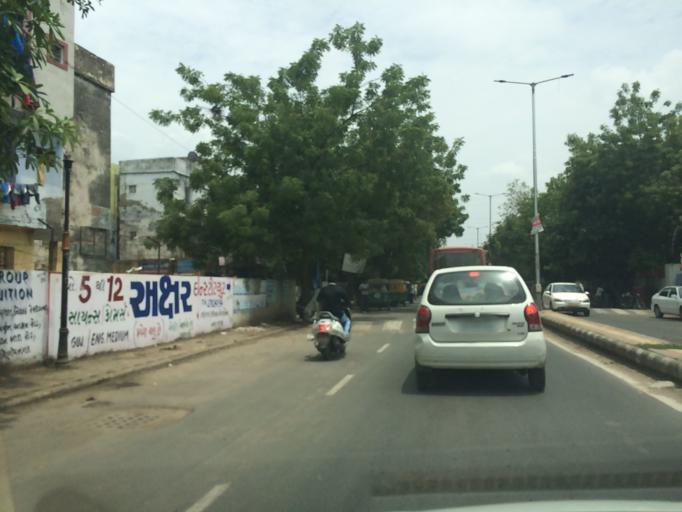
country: IN
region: Gujarat
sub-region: Ahmadabad
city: Ahmedabad
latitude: 23.0705
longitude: 72.5659
